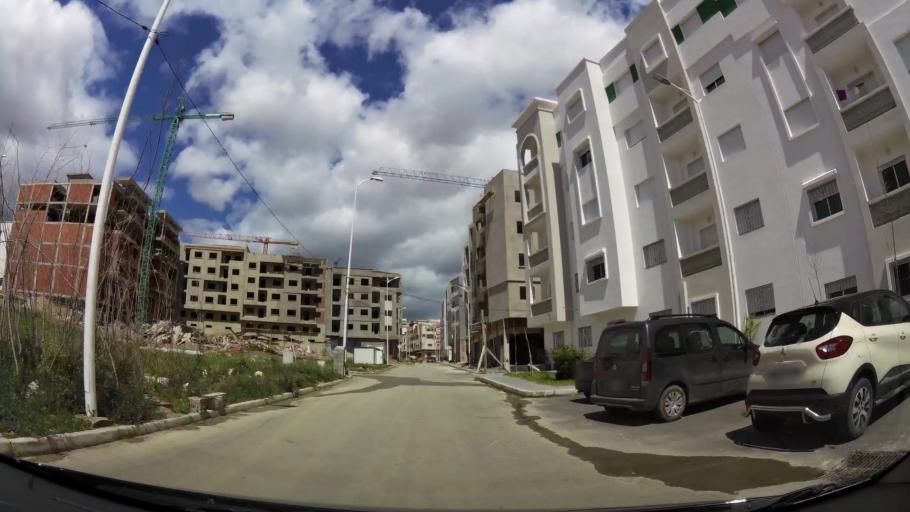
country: MA
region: Tanger-Tetouan
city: Tetouan
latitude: 35.5808
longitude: -5.3407
